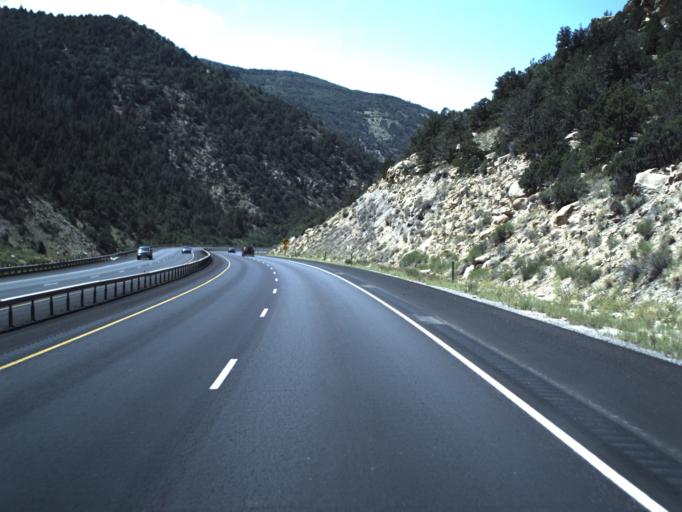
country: US
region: Utah
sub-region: Sevier County
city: Salina
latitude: 38.8827
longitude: -111.5885
